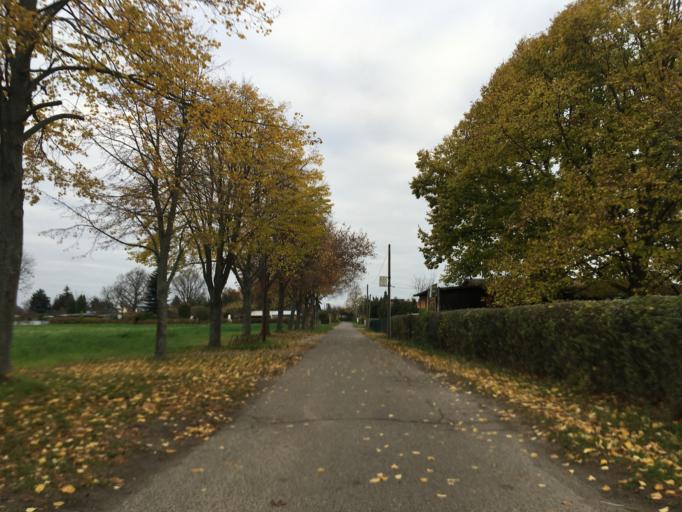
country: DE
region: Brandenburg
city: Vetschau
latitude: 51.7815
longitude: 14.0612
